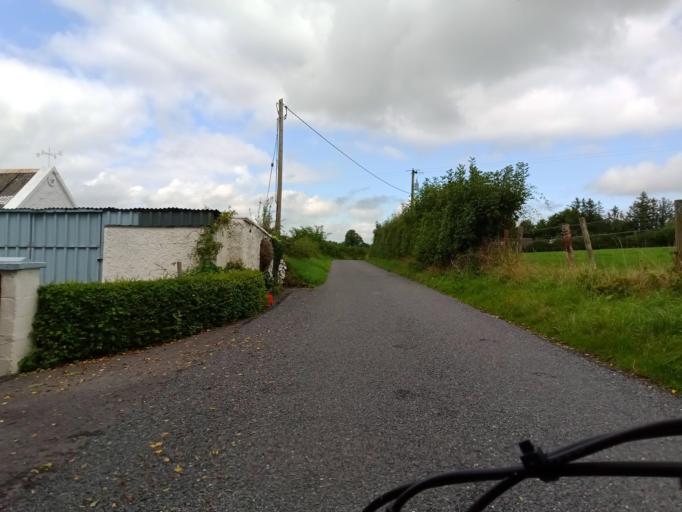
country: IE
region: Leinster
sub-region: Kilkenny
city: Callan
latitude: 52.5320
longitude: -7.2876
